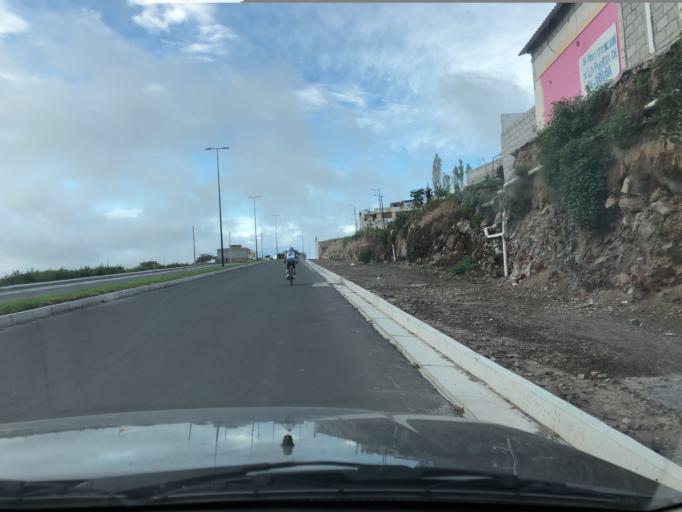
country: EC
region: Imbabura
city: Ibarra
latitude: 0.3502
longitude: -78.1409
